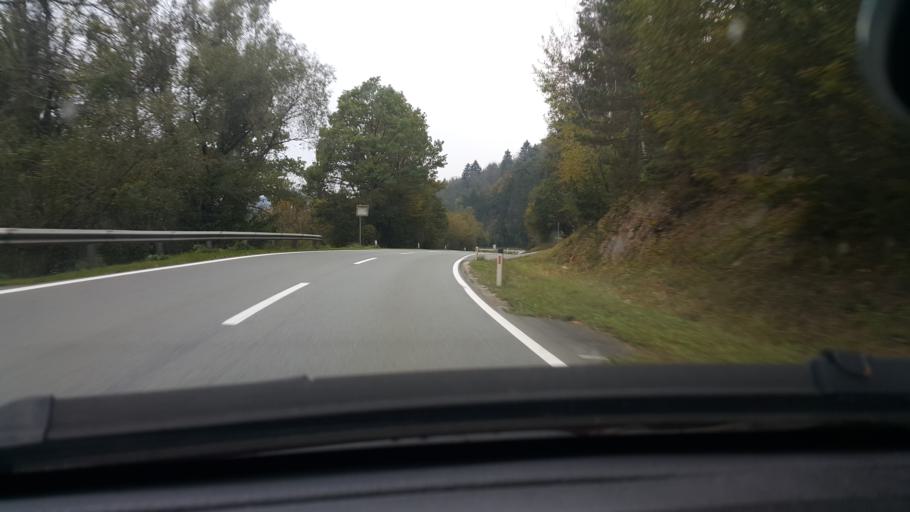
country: AT
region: Carinthia
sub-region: Politischer Bezirk Wolfsberg
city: Lavamund
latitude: 46.6218
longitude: 14.9731
